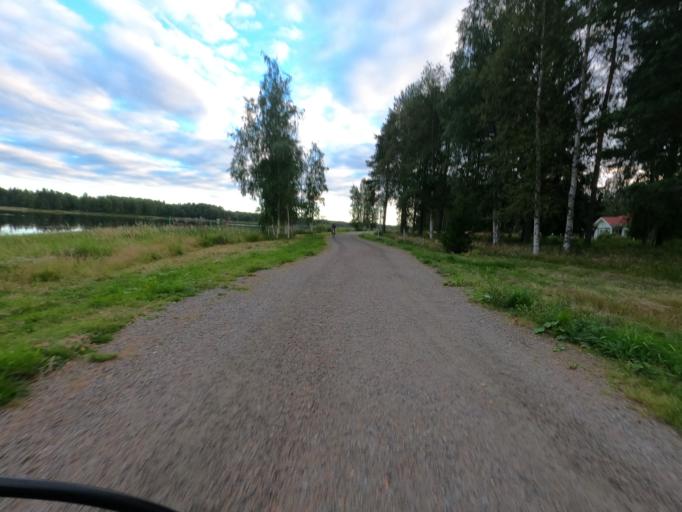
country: FI
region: North Karelia
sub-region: Joensuu
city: Joensuu
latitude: 62.6114
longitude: 29.8409
